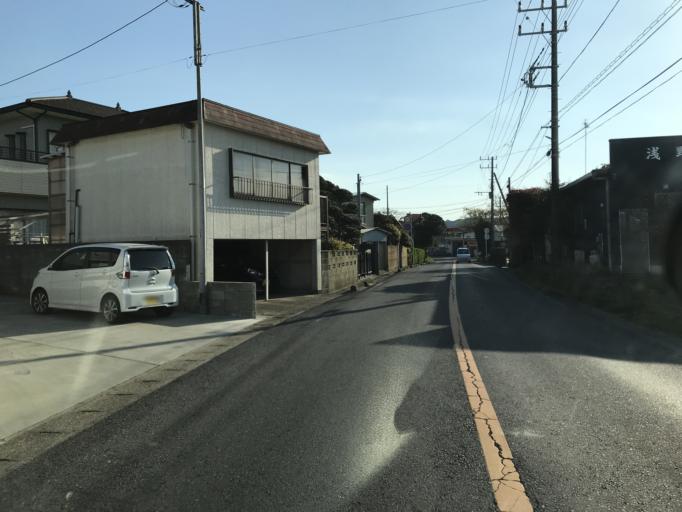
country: JP
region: Chiba
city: Asahi
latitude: 35.7282
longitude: 140.6875
